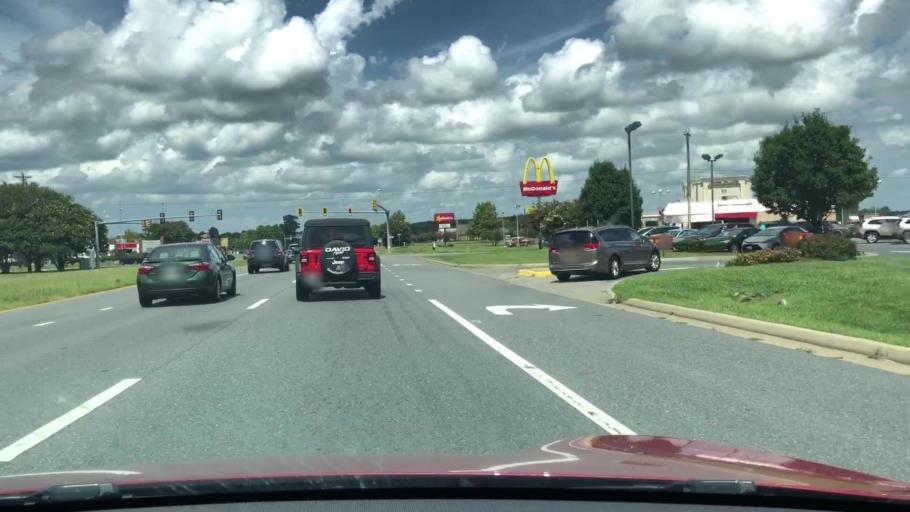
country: US
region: Virginia
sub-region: Northampton County
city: Exmore
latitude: 37.5202
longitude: -75.8315
